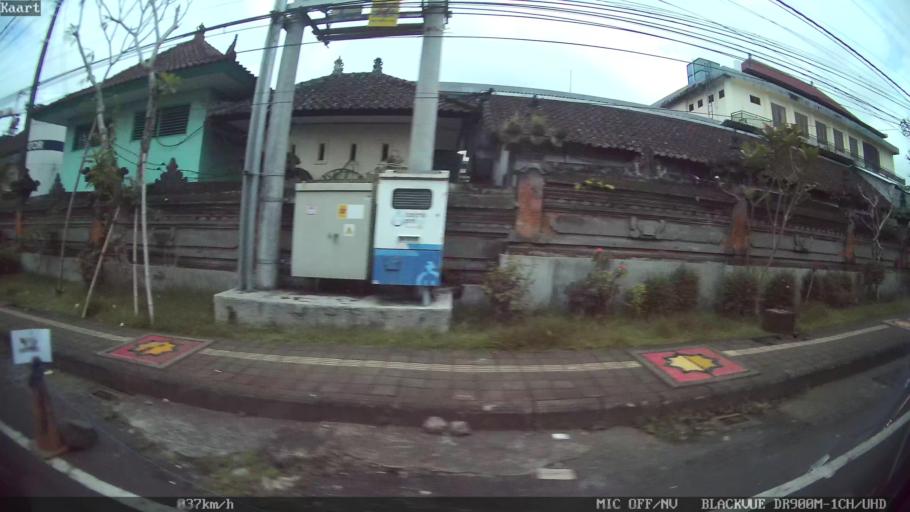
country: ID
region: Bali
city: Bangli
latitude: -8.4564
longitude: 115.3530
